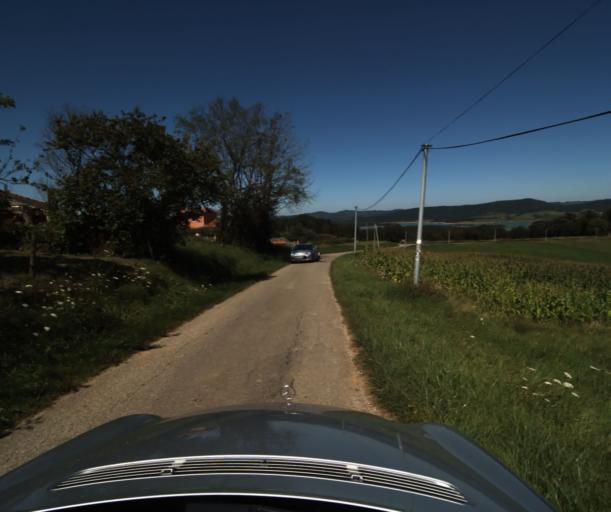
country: FR
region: Midi-Pyrenees
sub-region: Departement de l'Ariege
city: Belesta
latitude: 42.9609
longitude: 1.9328
